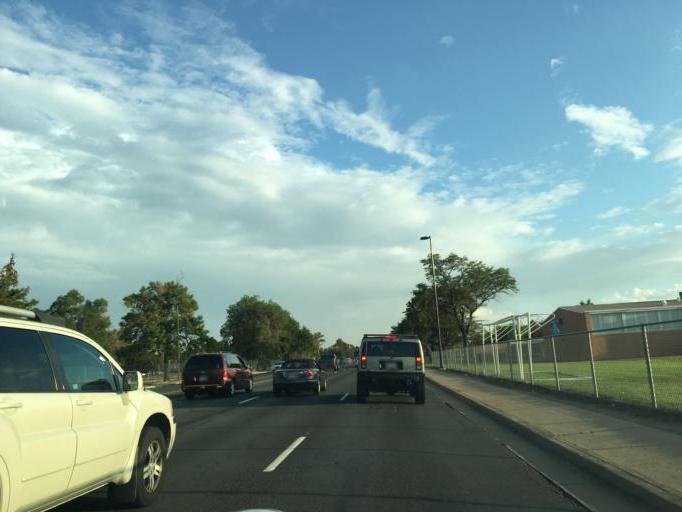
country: US
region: Colorado
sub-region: Adams County
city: Aurora
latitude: 39.7499
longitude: -104.8471
